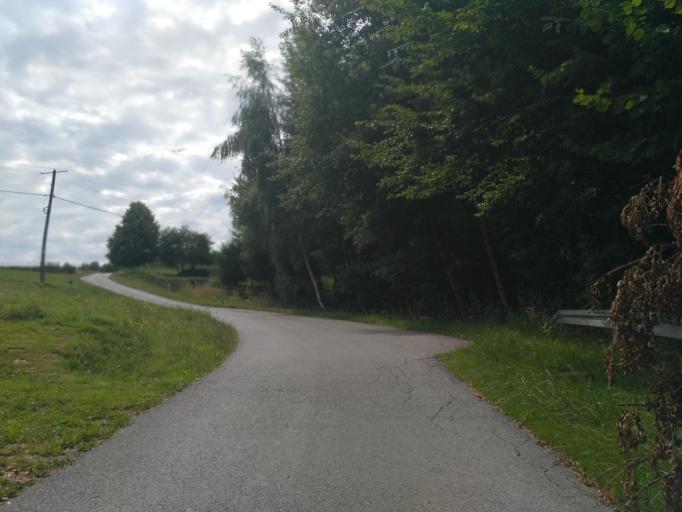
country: PL
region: Subcarpathian Voivodeship
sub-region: Powiat rzeszowski
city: Straszydle
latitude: 49.8919
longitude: 21.9811
